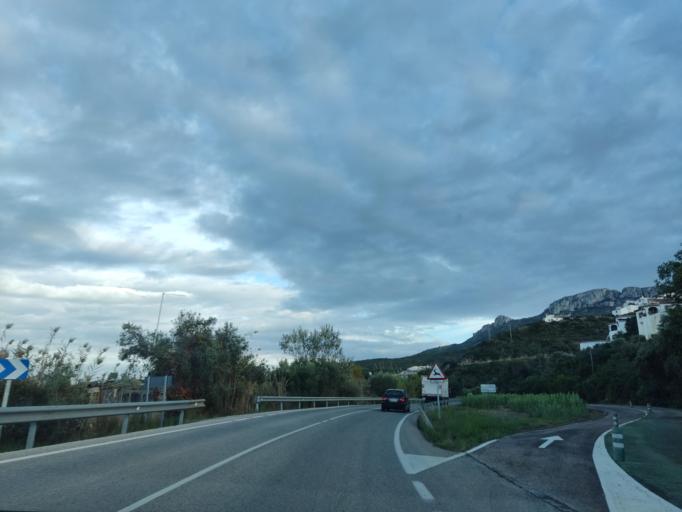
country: ES
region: Valencia
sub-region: Provincia de Alicante
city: Benimeli
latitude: 38.8529
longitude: -0.0461
